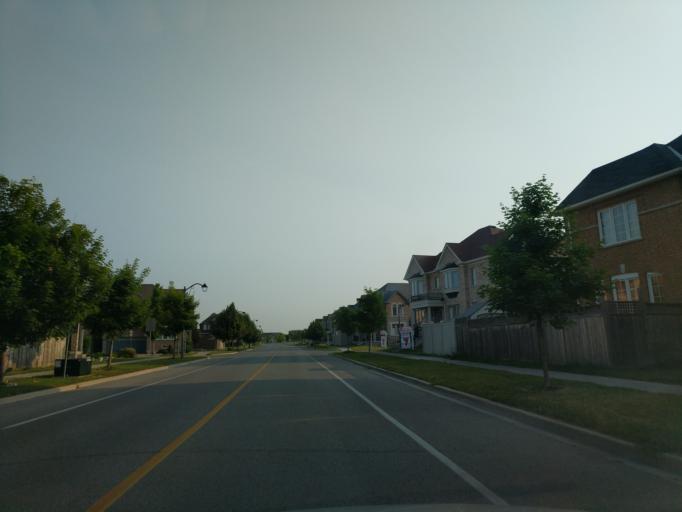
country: CA
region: Ontario
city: Markham
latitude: 43.8950
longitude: -79.2745
